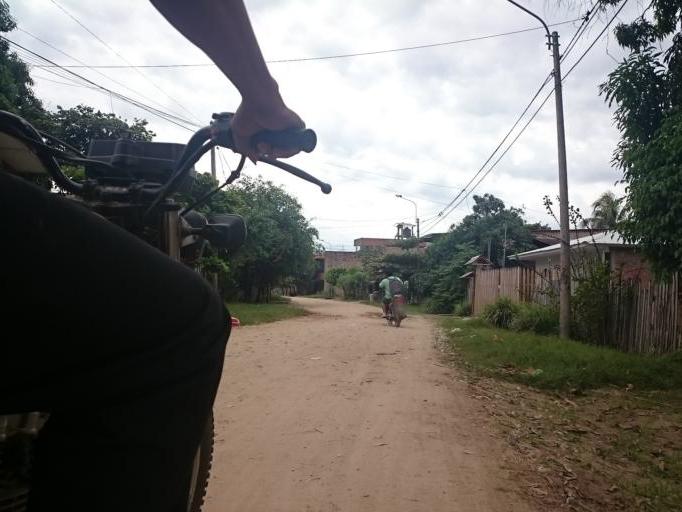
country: PE
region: Ucayali
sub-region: Provincia de Coronel Portillo
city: Pucallpa
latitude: -8.3794
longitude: -74.5412
